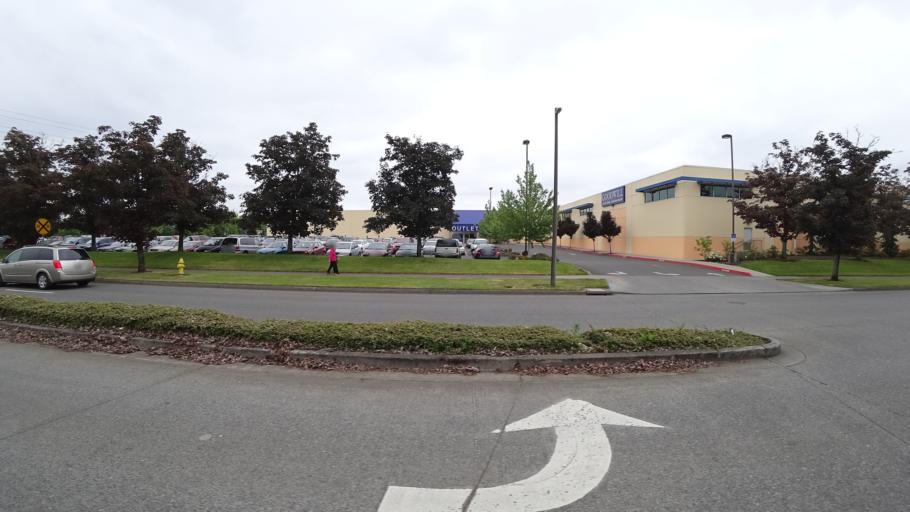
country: US
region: Oregon
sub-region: Washington County
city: Aloha
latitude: 45.4981
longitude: -122.9177
